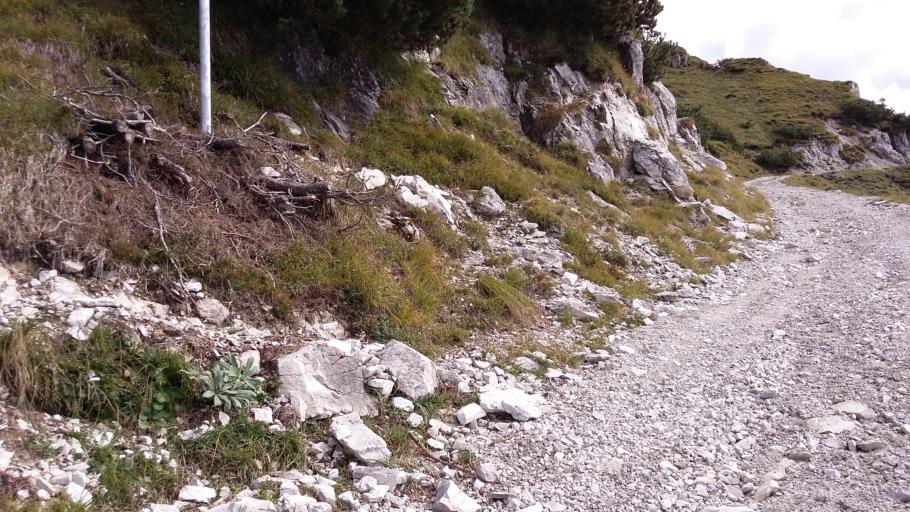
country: IT
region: Lombardy
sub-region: Provincia di Brescia
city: Magasa
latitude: 45.8033
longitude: 10.6073
